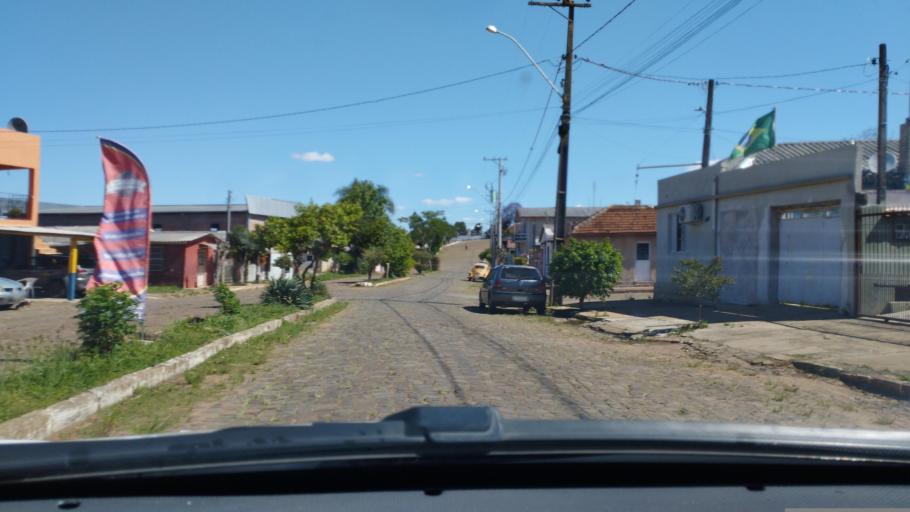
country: BR
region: Rio Grande do Sul
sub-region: Tupancireta
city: Tupancireta
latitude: -29.0888
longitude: -53.8347
